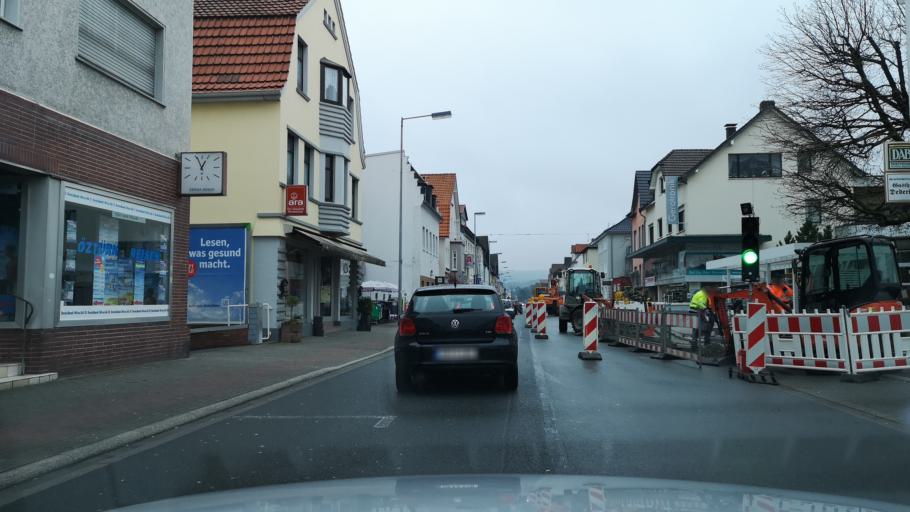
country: DE
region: North Rhine-Westphalia
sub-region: Regierungsbezirk Arnsberg
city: Menden
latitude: 51.4138
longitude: 7.8317
